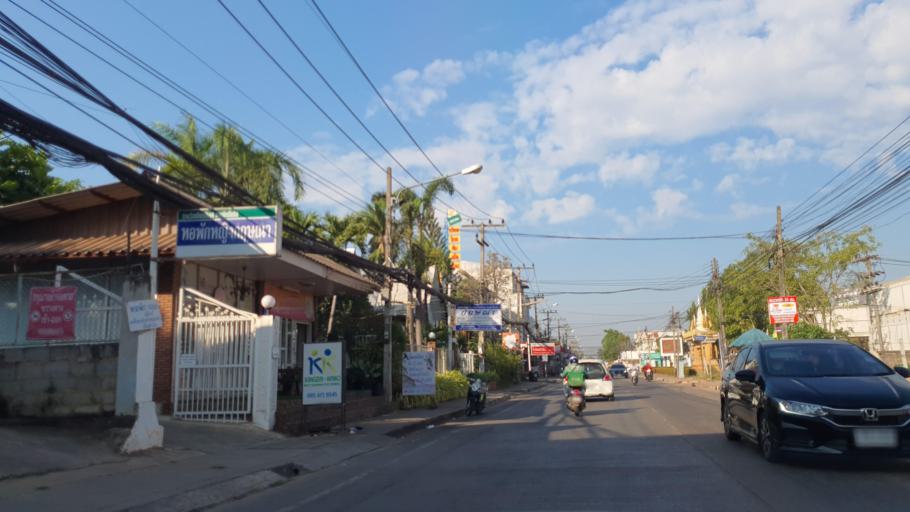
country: TH
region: Khon Kaen
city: Khon Kaen
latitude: 16.4214
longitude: 102.8173
